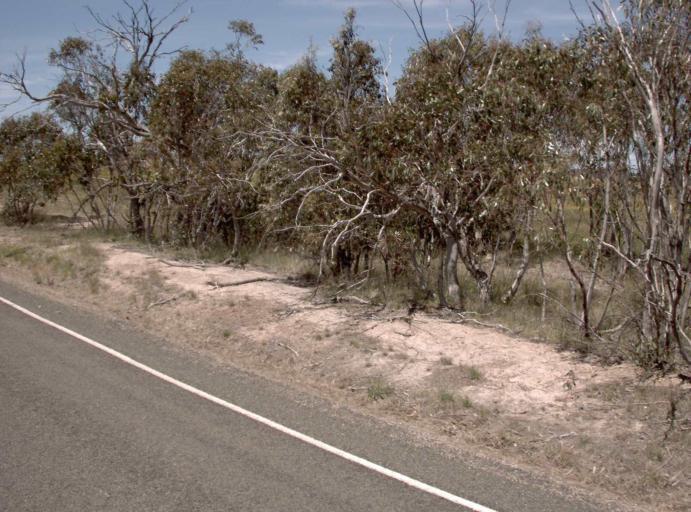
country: AU
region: Victoria
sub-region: Alpine
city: Mount Beauty
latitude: -37.1260
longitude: 147.6376
